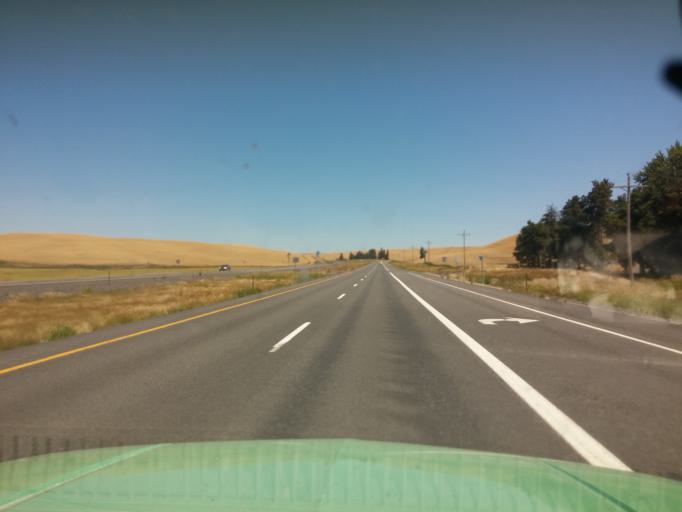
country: US
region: Idaho
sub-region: Nez Perce County
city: Lewiston
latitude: 46.4926
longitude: -117.0134
